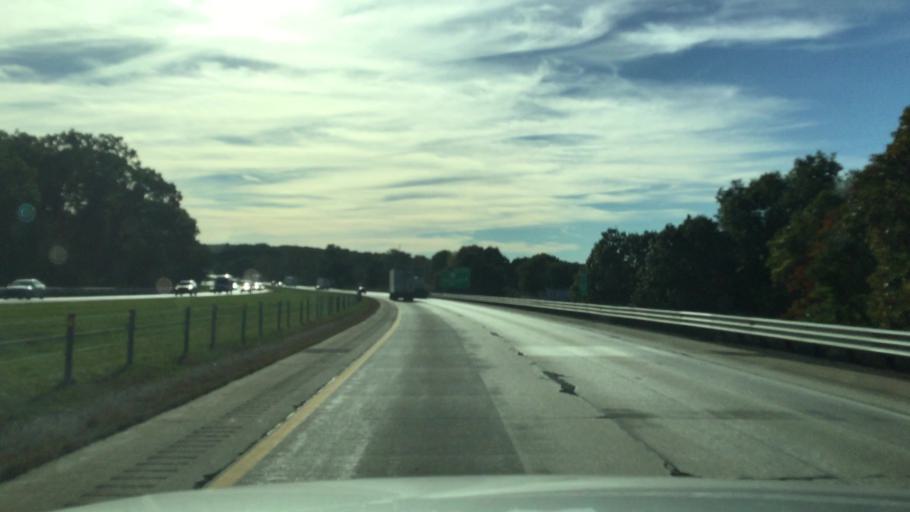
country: US
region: Michigan
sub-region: Calhoun County
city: Brownlee Park
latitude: 42.2849
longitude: -85.1486
